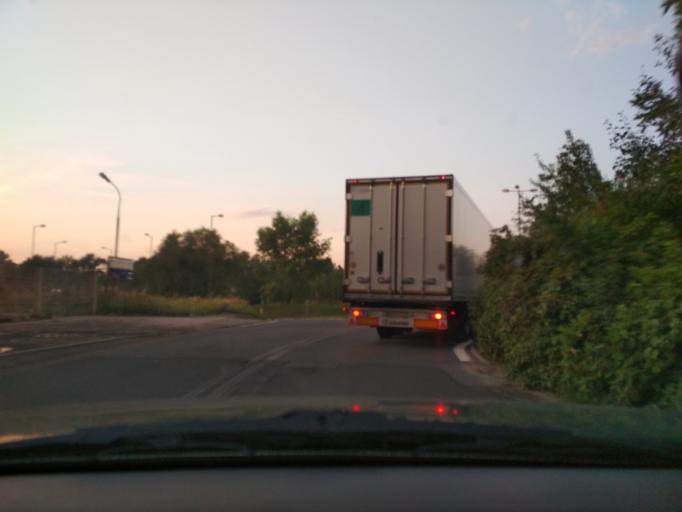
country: PL
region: Silesian Voivodeship
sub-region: Gliwice
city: Gliwice
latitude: 50.2701
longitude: 18.7029
